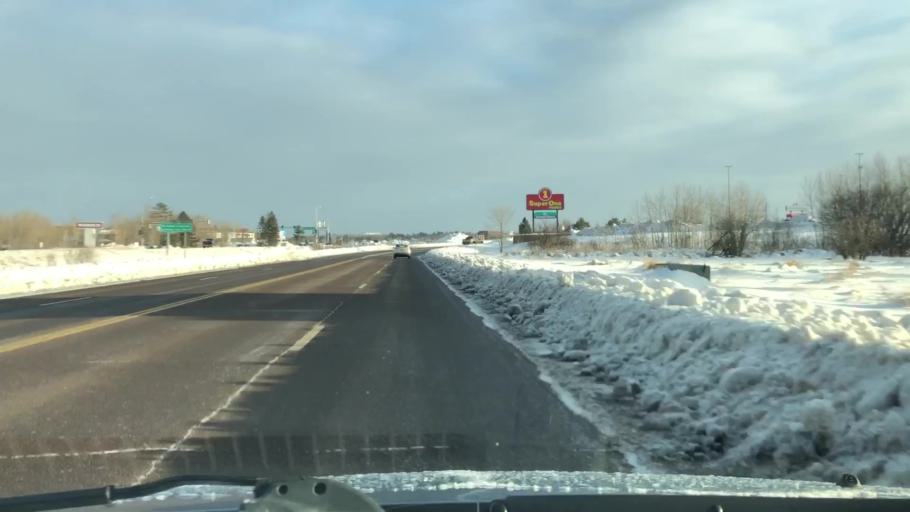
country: US
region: Minnesota
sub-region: Saint Louis County
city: Hermantown
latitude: 46.8120
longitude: -92.1711
